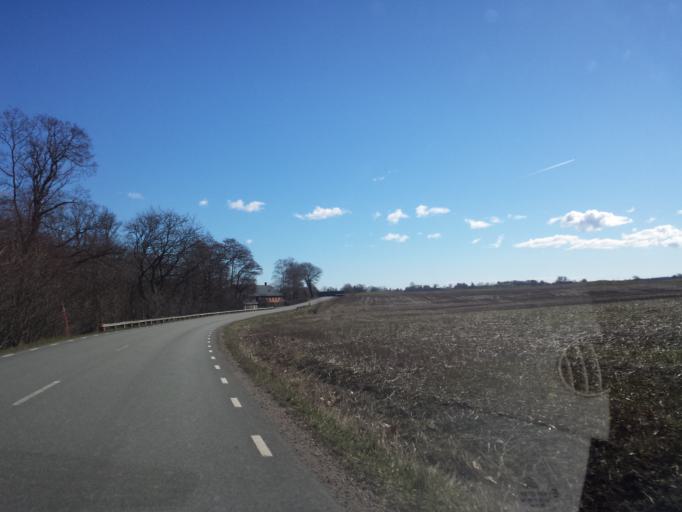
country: SE
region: Skane
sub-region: Sjobo Kommun
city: Sjoebo
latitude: 55.6225
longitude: 13.8367
